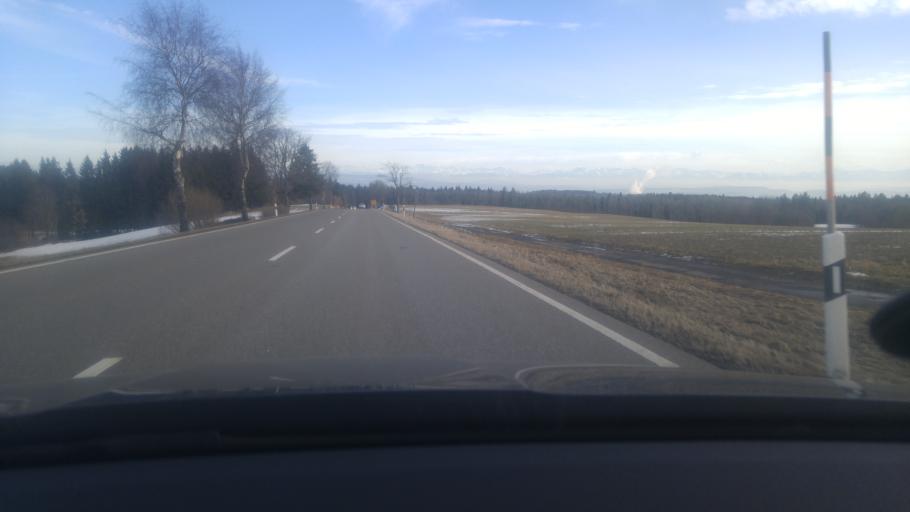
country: DE
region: Baden-Wuerttemberg
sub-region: Freiburg Region
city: Hochenschwand
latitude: 47.6932
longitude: 8.1511
